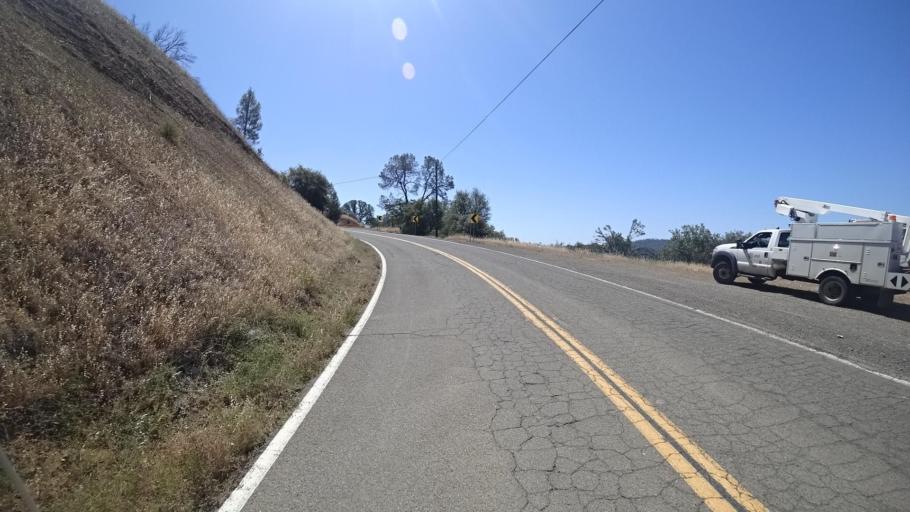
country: US
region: California
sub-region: Lake County
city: Hidden Valley Lake
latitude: 38.8784
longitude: -122.5292
